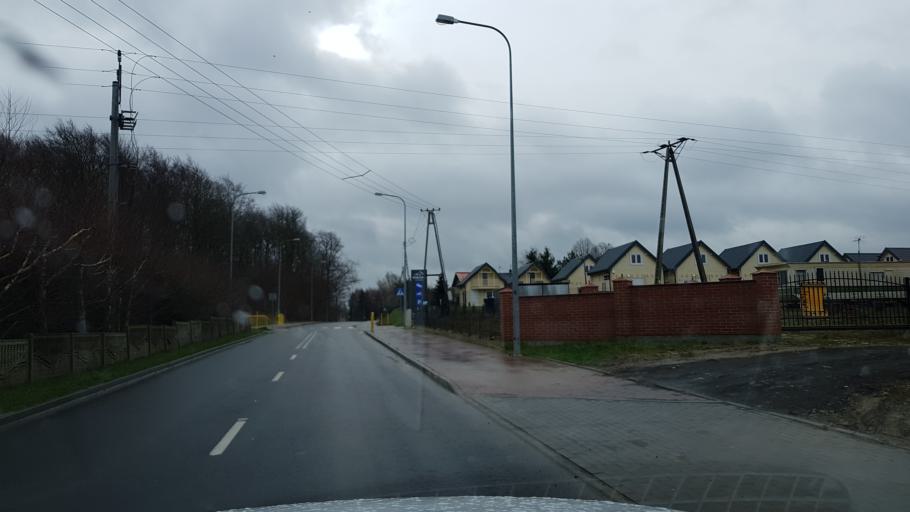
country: PL
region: West Pomeranian Voivodeship
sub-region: Powiat kolobrzeski
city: Ustronie Morskie
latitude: 54.2081
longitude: 15.7665
